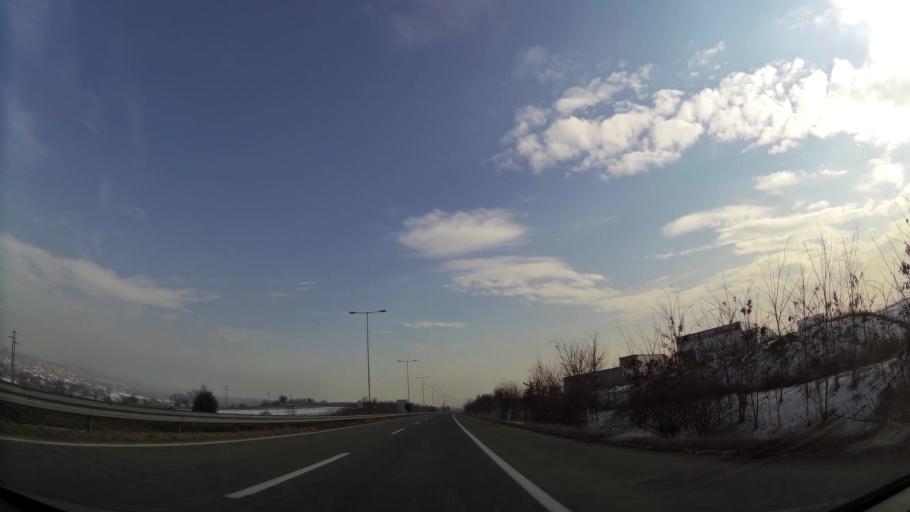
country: MK
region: Suto Orizari
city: Suto Orizare
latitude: 42.0504
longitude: 21.4305
